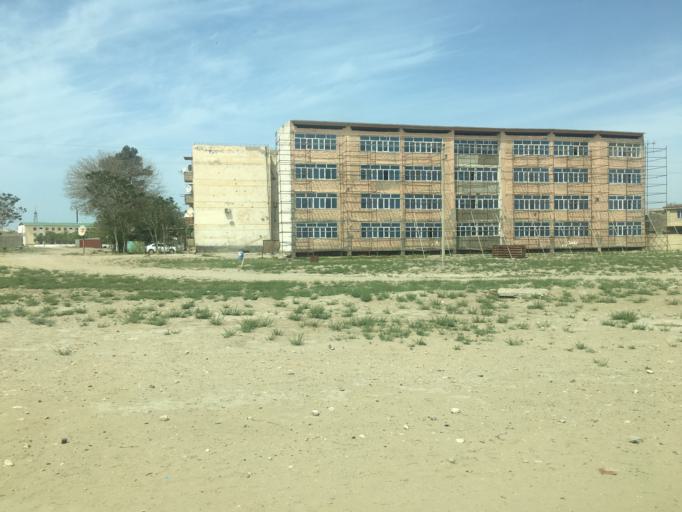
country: TM
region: Balkan
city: Turkmenbasy
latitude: 39.4038
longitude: 53.1380
